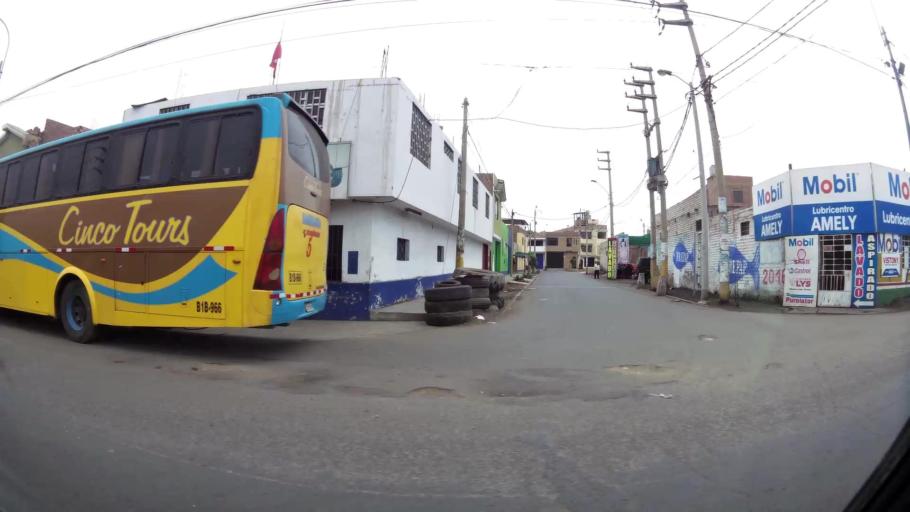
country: PE
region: Lima
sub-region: Barranca
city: Barranca
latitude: -10.7577
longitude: -77.7556
